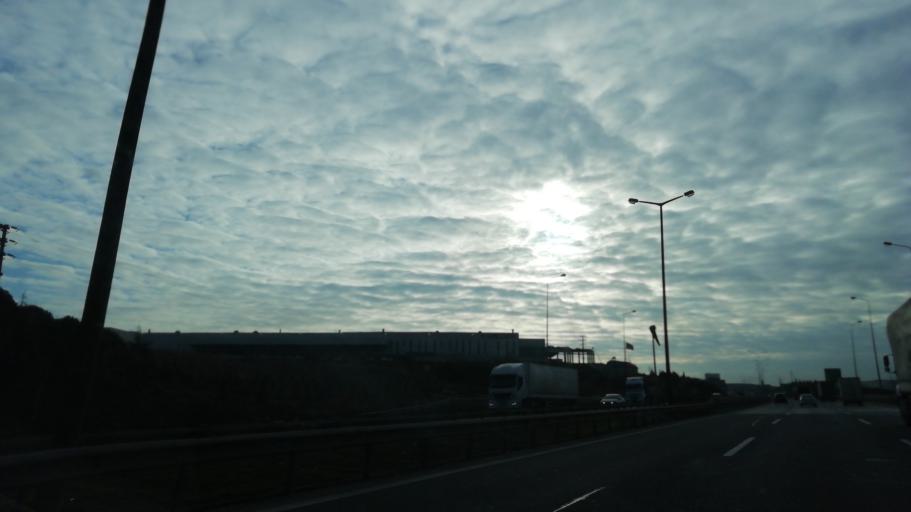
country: TR
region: Kocaeli
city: Balcik
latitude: 40.8660
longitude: 29.3990
